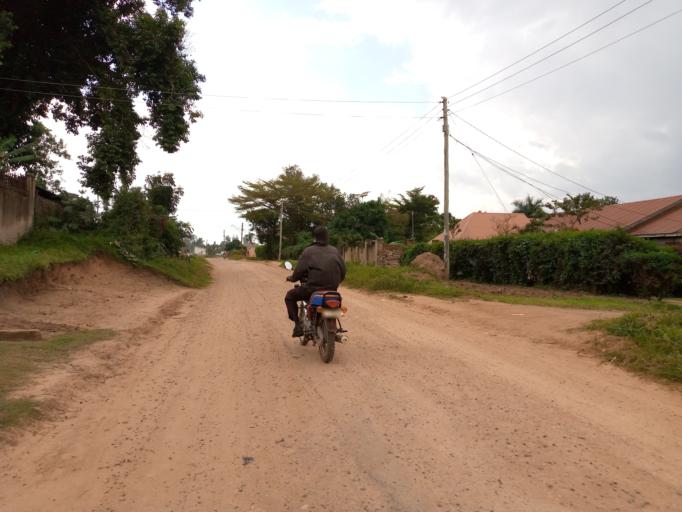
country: UG
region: Eastern Region
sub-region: Mbale District
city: Mbale
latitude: 1.0827
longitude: 34.1750
